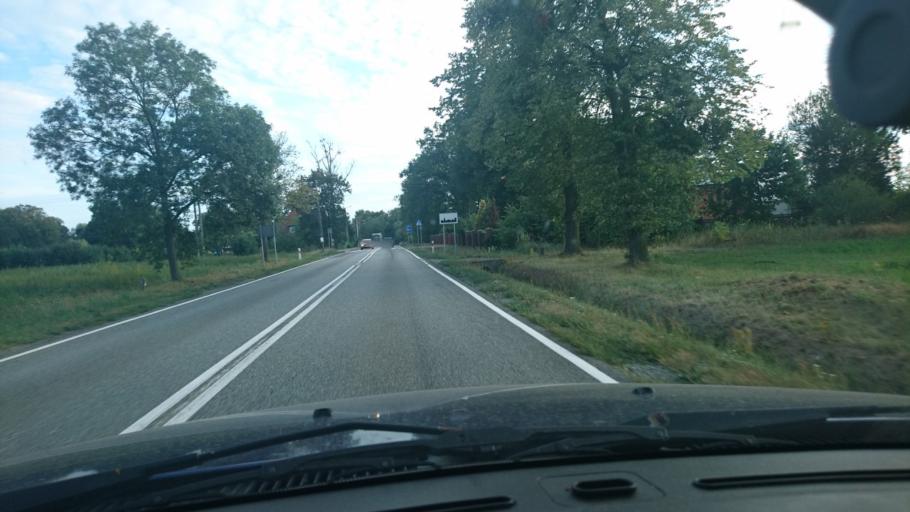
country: PL
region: Opole Voivodeship
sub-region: Powiat kluczborski
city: Byczyna
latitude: 51.0659
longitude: 18.2022
